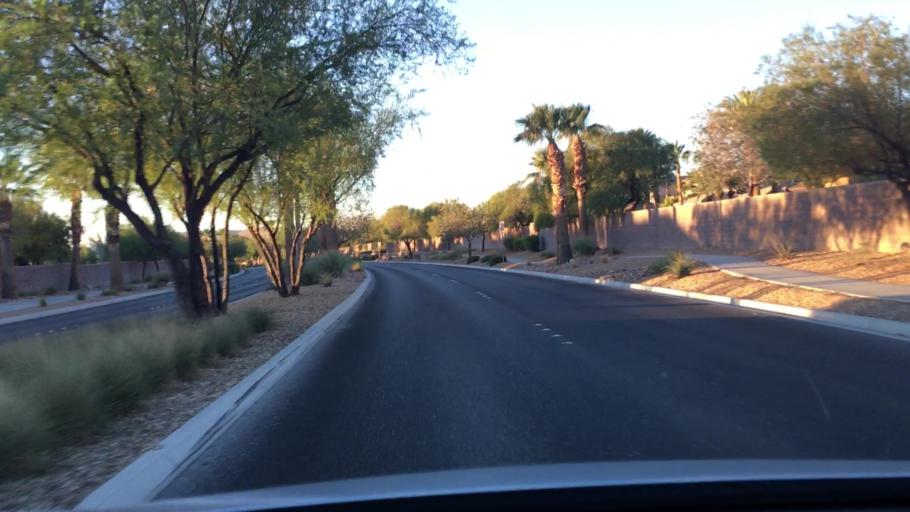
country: US
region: Nevada
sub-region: Clark County
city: Summerlin South
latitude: 36.1327
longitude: -115.3430
